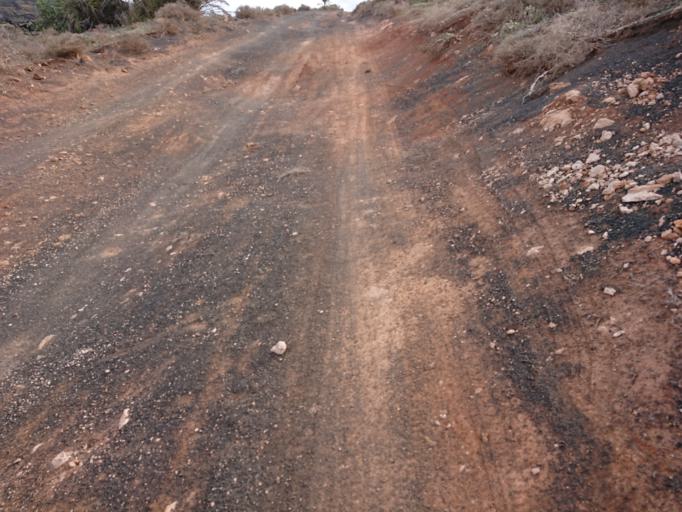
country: ES
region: Canary Islands
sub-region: Provincia de Las Palmas
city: Tinajo
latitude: 29.0197
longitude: -13.6765
